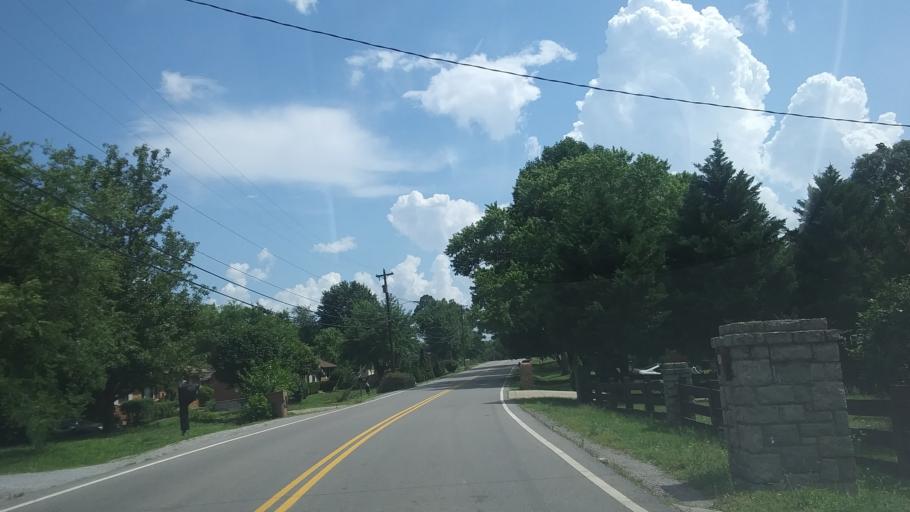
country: US
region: Tennessee
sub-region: Davidson County
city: Oak Hill
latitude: 36.0778
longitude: -86.7027
